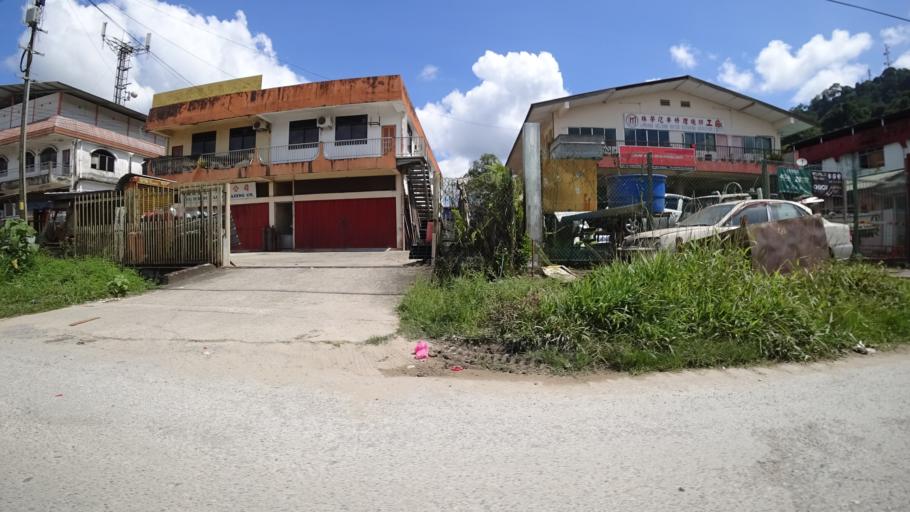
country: MY
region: Sarawak
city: Limbang
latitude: 4.7418
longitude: 115.0022
